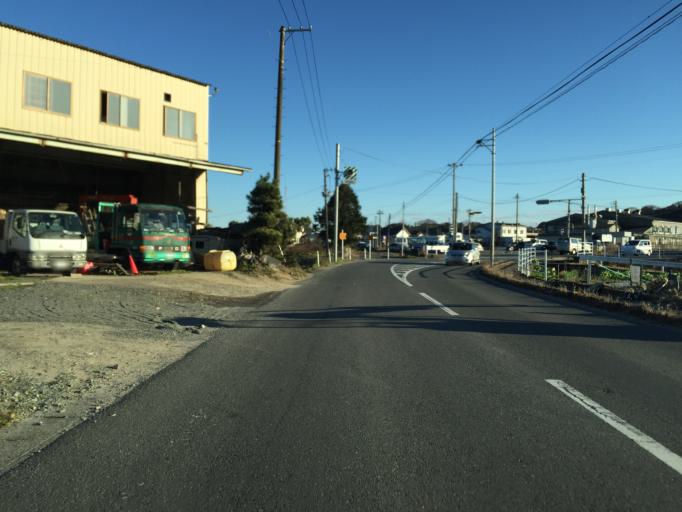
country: JP
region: Fukushima
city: Iwaki
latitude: 37.0706
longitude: 140.8782
